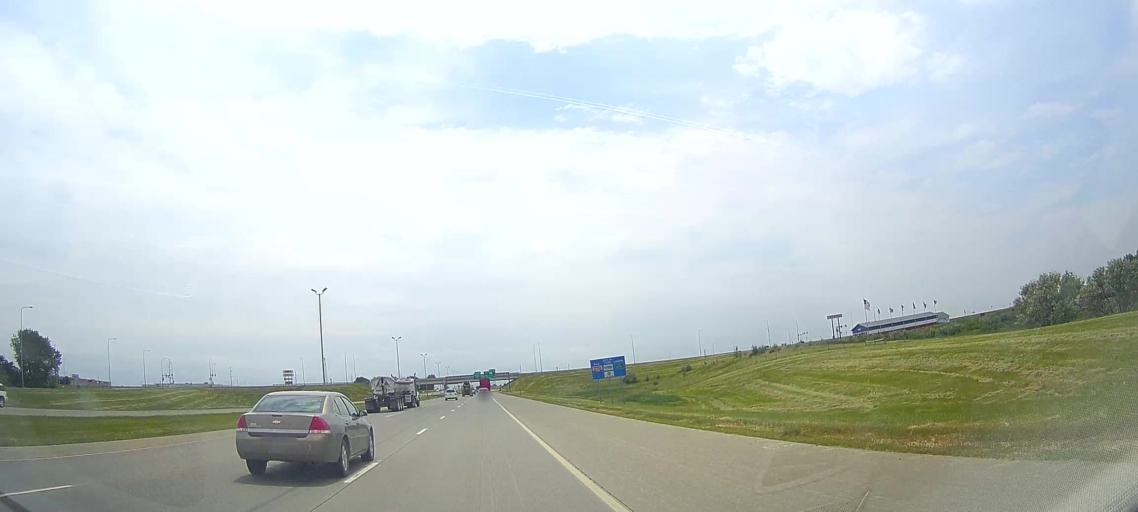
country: US
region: South Dakota
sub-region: Minnehaha County
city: Crooks
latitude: 43.6048
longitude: -96.7712
